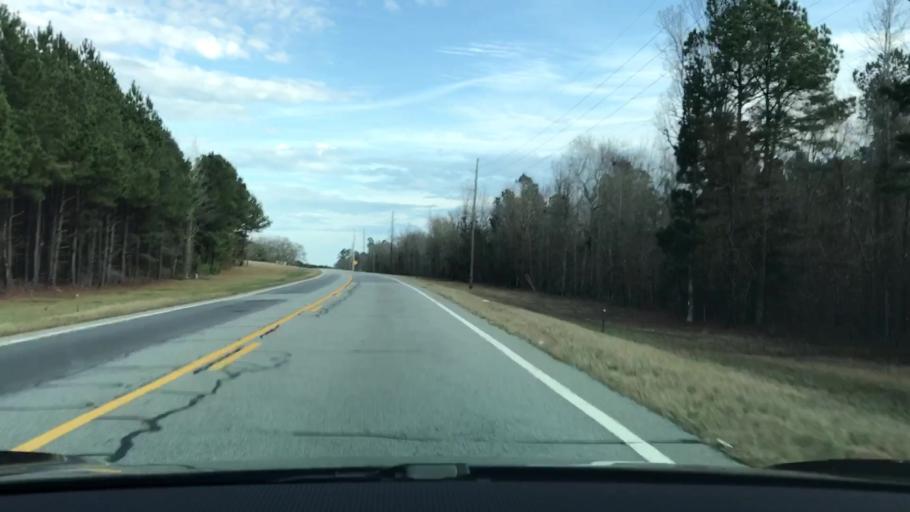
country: US
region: Georgia
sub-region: Warren County
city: Warrenton
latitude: 33.3891
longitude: -82.6424
